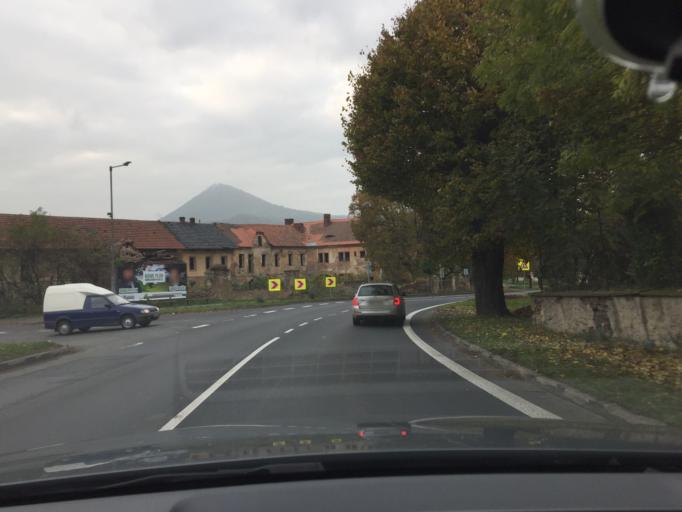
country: CZ
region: Ustecky
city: Velemin
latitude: 50.5370
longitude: 13.9783
